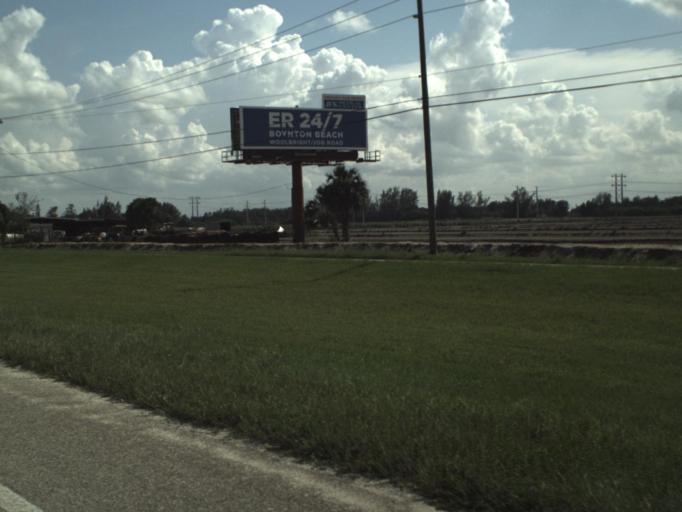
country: US
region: Florida
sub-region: Palm Beach County
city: Villages of Oriole
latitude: 26.4894
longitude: -80.2051
